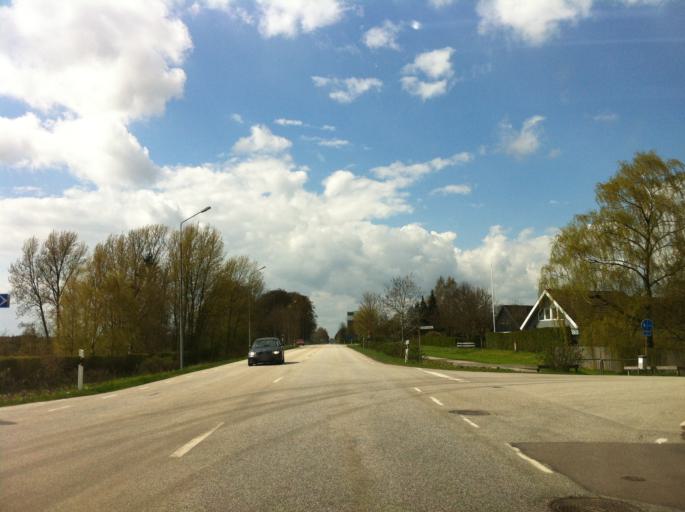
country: SE
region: Skane
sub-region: Eslovs Kommun
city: Stehag
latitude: 55.8510
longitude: 13.4152
